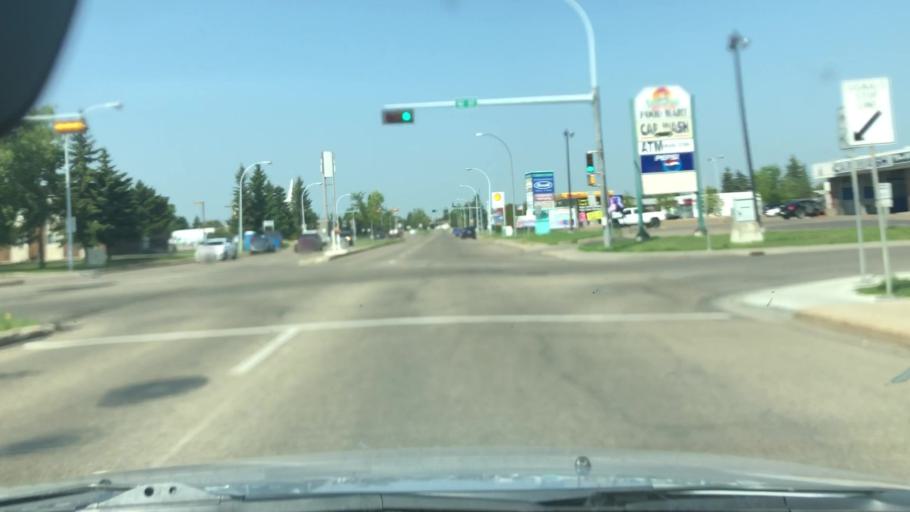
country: CA
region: Alberta
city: Edmonton
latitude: 53.6059
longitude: -113.4822
